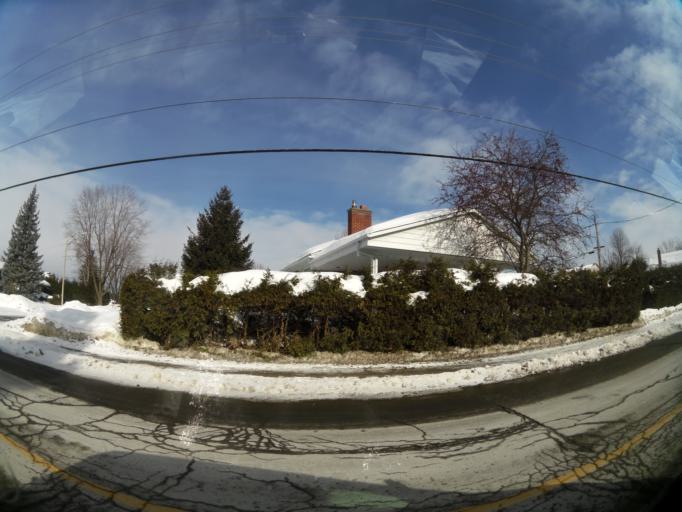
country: CA
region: Quebec
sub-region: Outaouais
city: Gatineau
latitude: 45.4809
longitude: -75.6205
